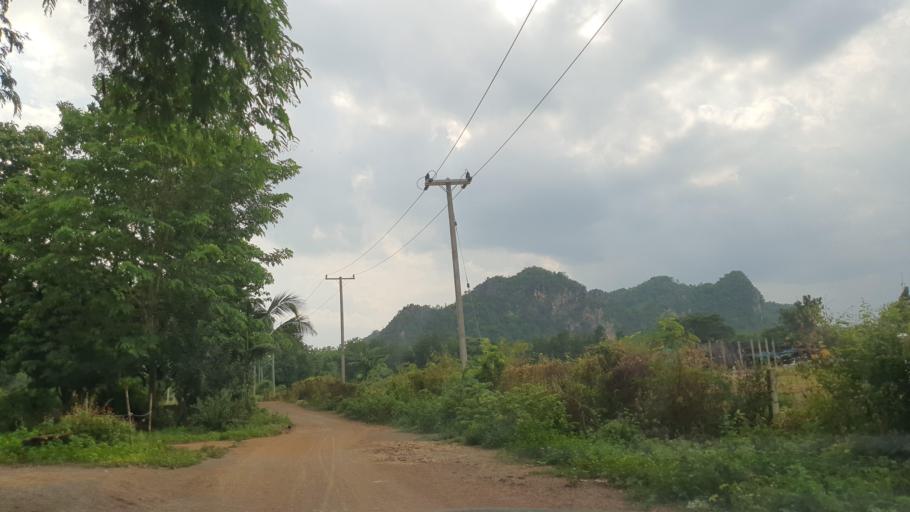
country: TH
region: Sukhothai
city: Thung Saliam
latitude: 17.2504
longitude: 99.5472
